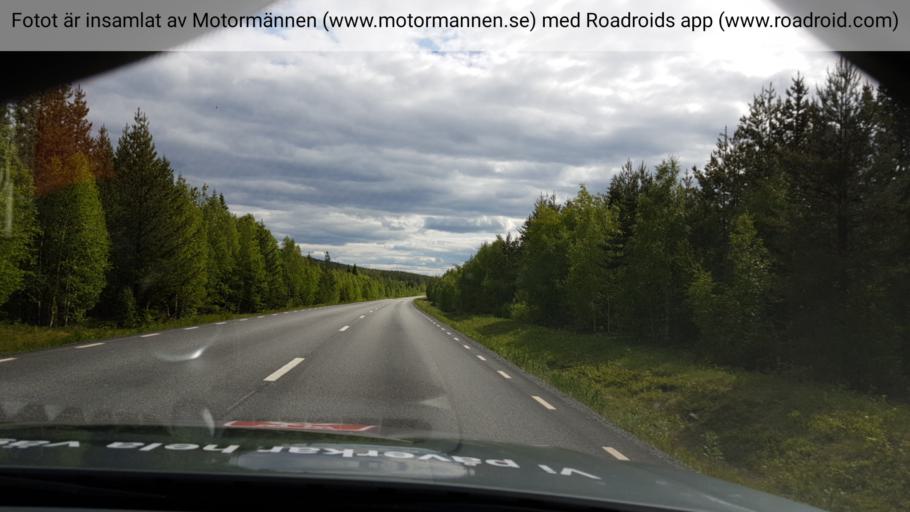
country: SE
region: Jaemtland
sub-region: Stroemsunds Kommun
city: Stroemsund
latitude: 64.0375
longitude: 15.5380
